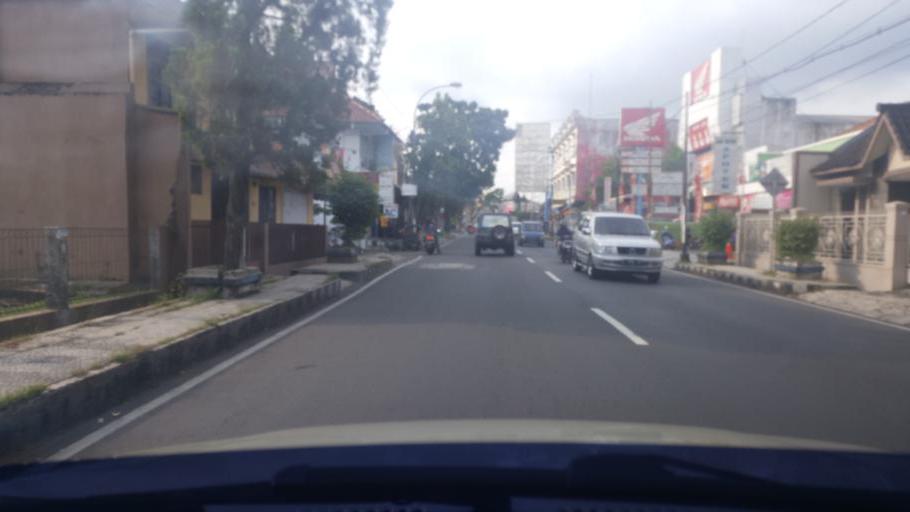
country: ID
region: West Java
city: Tawangsari
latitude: -7.3181
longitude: 108.2188
